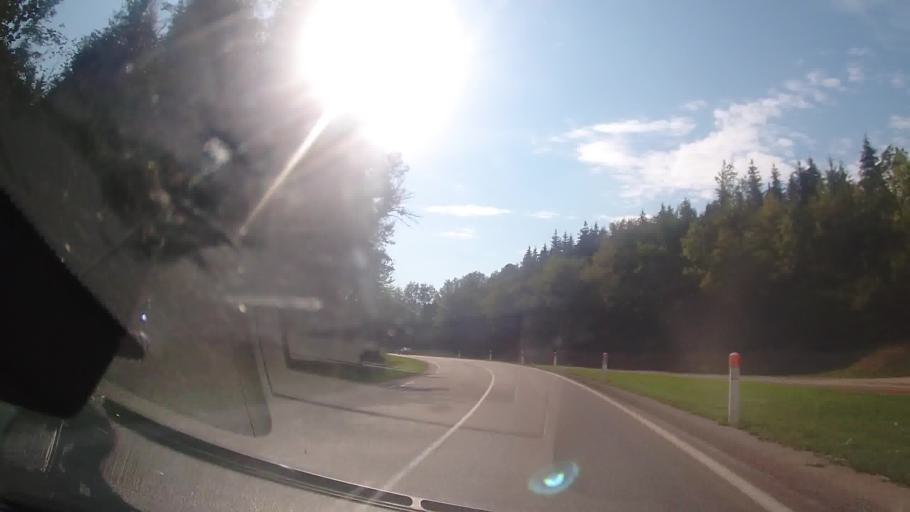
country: FR
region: Franche-Comte
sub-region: Departement du Jura
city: Clairvaux-les-Lacs
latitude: 46.5841
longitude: 5.8079
